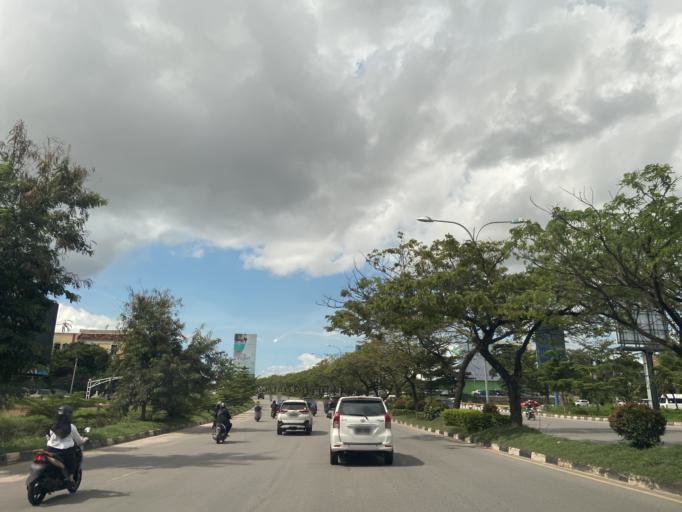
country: SG
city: Singapore
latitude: 1.1288
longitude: 104.0371
